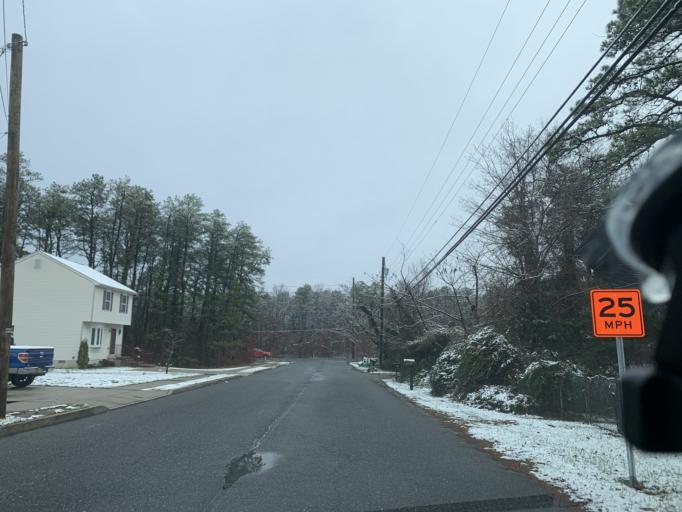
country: US
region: New Jersey
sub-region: Atlantic County
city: Pomona
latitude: 39.4348
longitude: -74.5949
